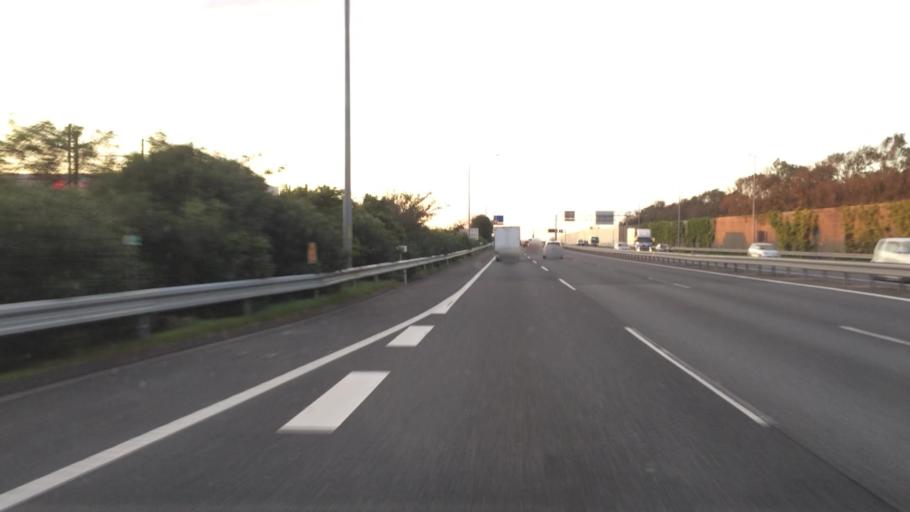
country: JP
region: Chiba
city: Funabashi
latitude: 35.6640
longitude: 140.0193
